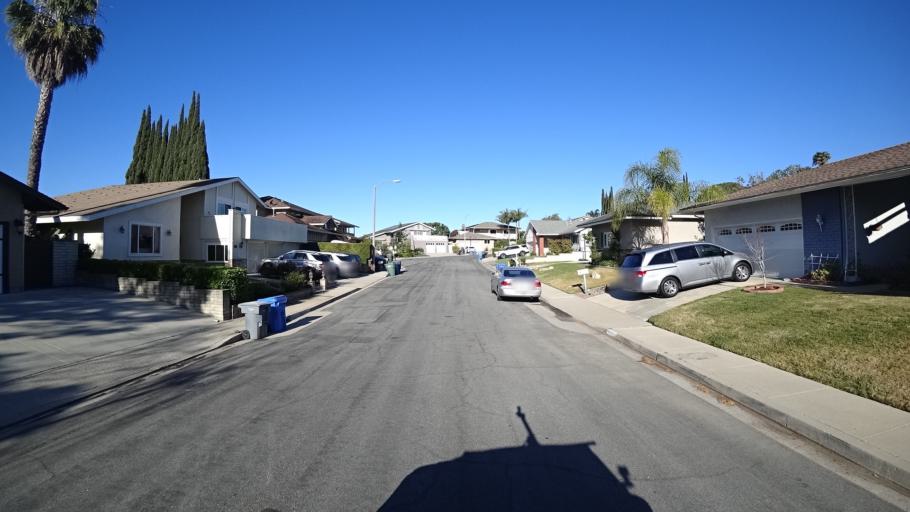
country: US
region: California
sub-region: Ventura County
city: Casa Conejo
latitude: 34.2147
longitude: -118.8955
